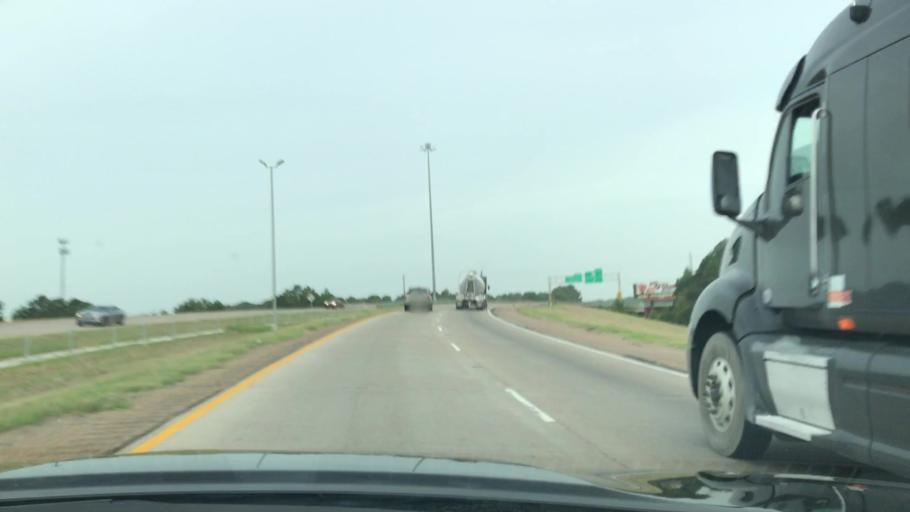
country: US
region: Louisiana
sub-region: Bossier Parish
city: Bossier City
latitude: 32.4156
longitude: -93.7862
